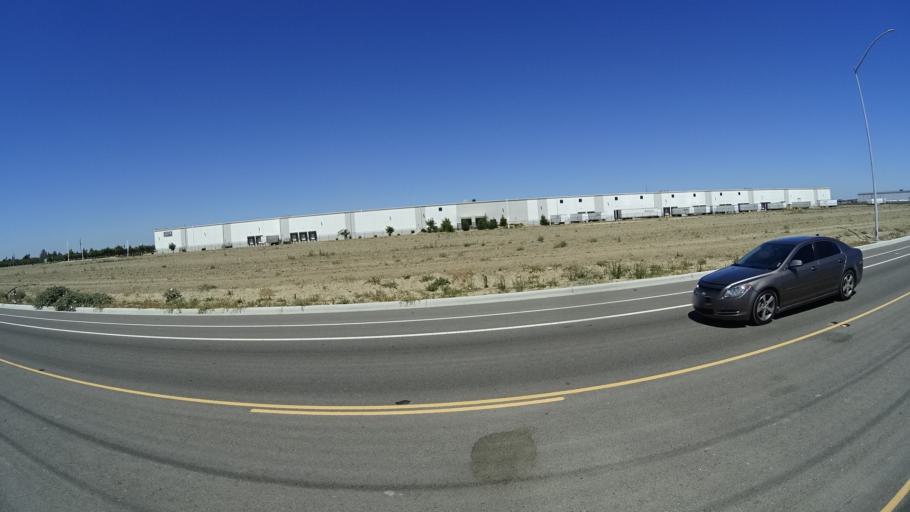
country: US
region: California
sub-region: Fresno County
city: Easton
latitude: 36.6800
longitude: -119.7726
